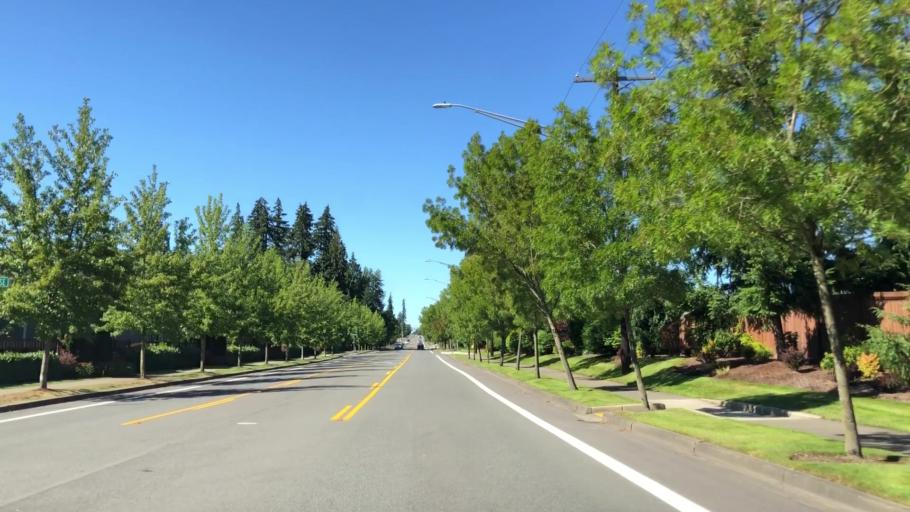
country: US
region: Washington
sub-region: Snohomish County
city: North Creek
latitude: 47.7982
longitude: -122.1810
